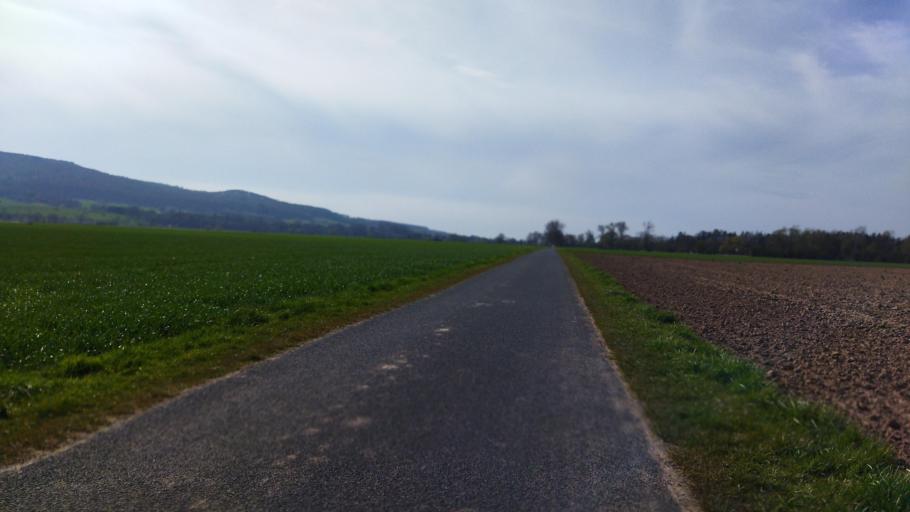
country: DE
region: Lower Saxony
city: Hessisch Oldendorf
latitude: 52.1654
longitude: 9.2063
